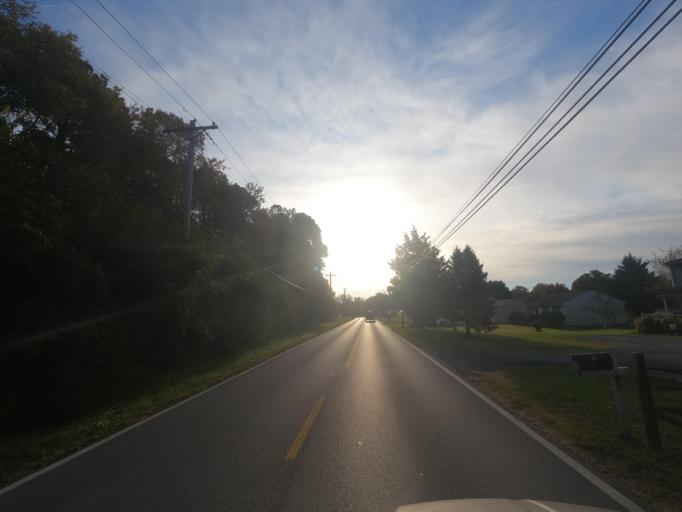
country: US
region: Maryland
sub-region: Calvert County
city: Lusby
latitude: 38.3871
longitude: -76.4282
